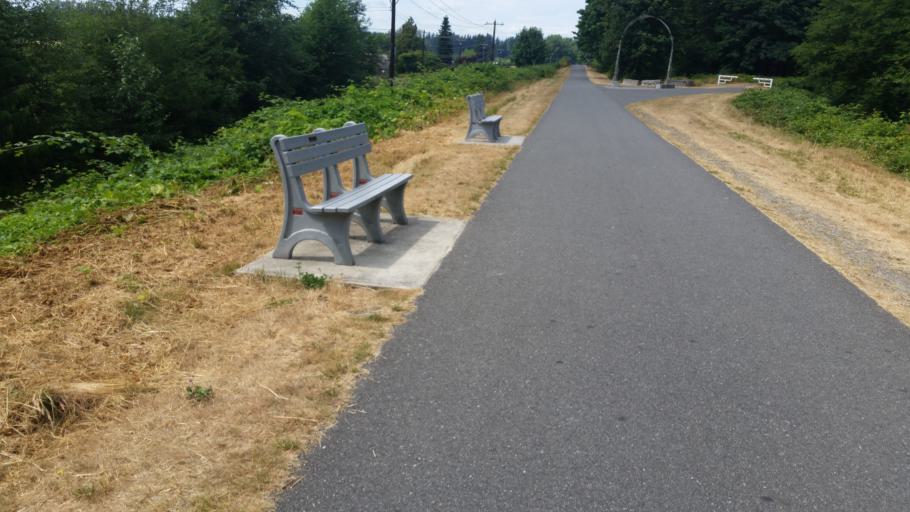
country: US
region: Washington
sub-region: Snohomish County
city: Arlington
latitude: 48.2054
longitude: -122.1291
